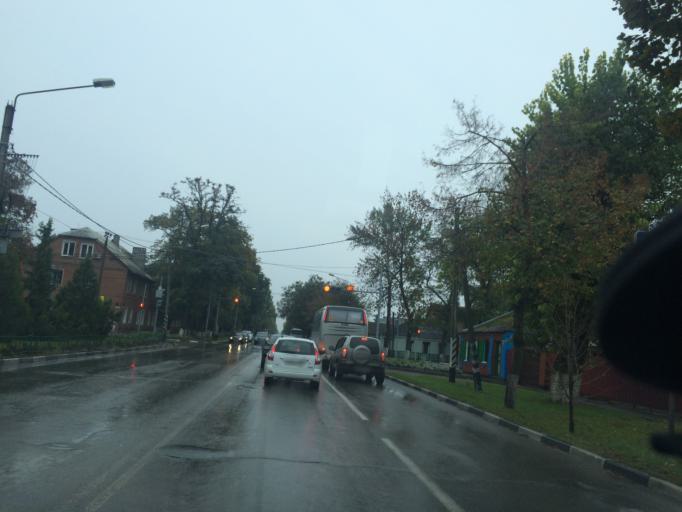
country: RU
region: Rostov
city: Azov
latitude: 47.0996
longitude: 39.4409
